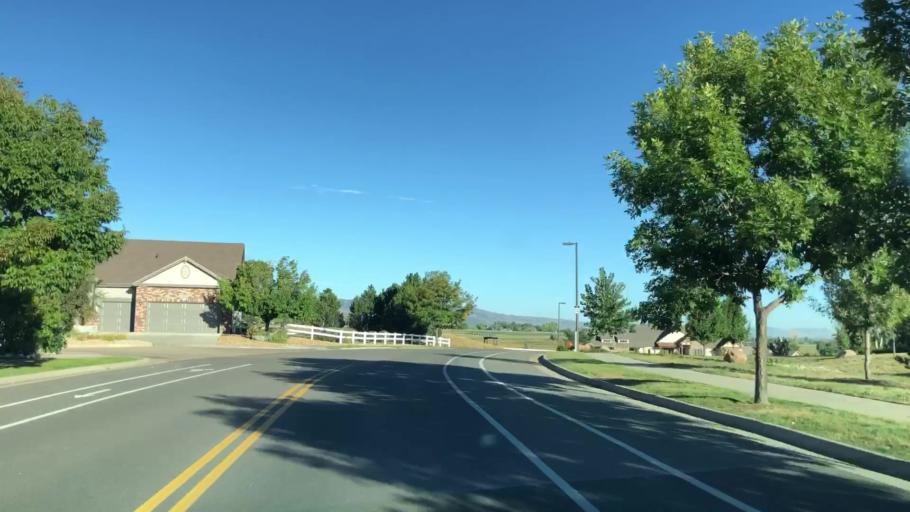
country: US
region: Colorado
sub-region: Larimer County
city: Loveland
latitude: 40.4620
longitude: -105.0359
